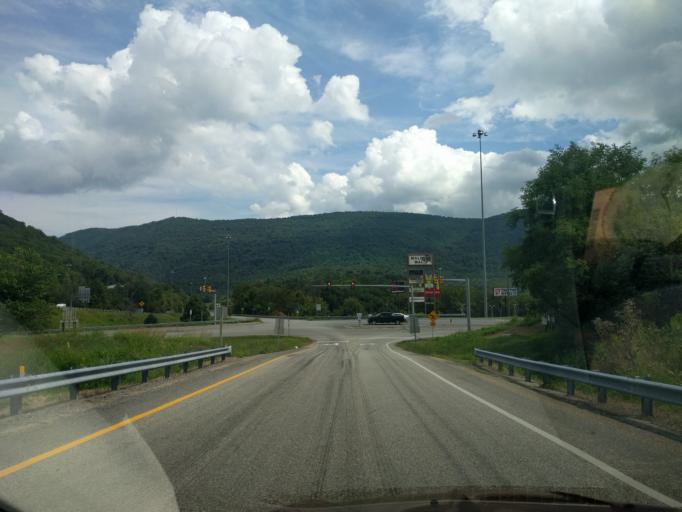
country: US
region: Virginia
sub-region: City of Covington
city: Fairlawn
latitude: 37.7747
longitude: -79.9687
